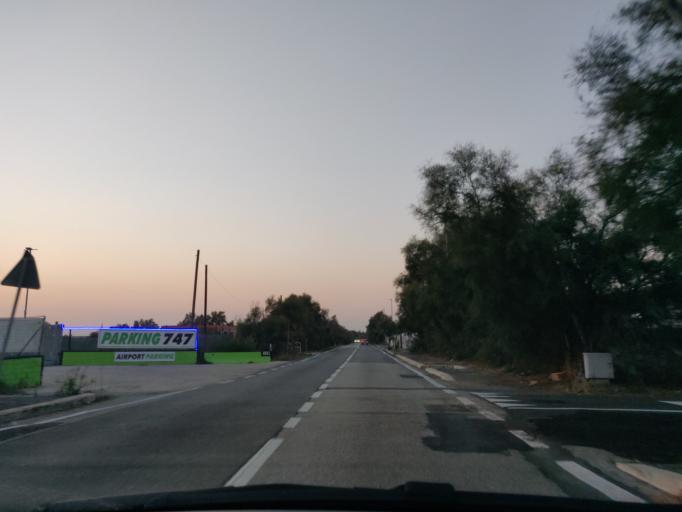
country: IT
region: Latium
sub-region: Citta metropolitana di Roma Capitale
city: Npp 23 (Parco Leonardo)
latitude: 41.8207
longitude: 12.2941
